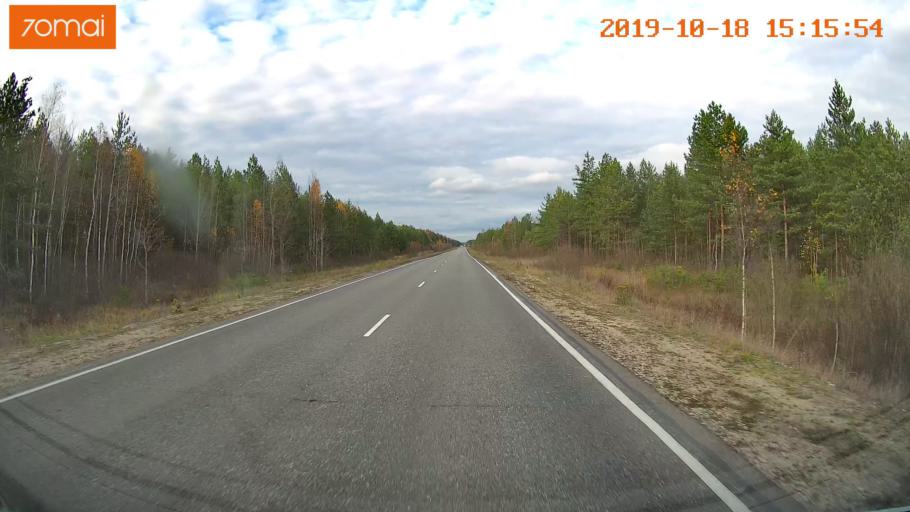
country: RU
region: Vladimir
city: Gus'-Khrustal'nyy
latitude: 55.6267
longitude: 40.7235
